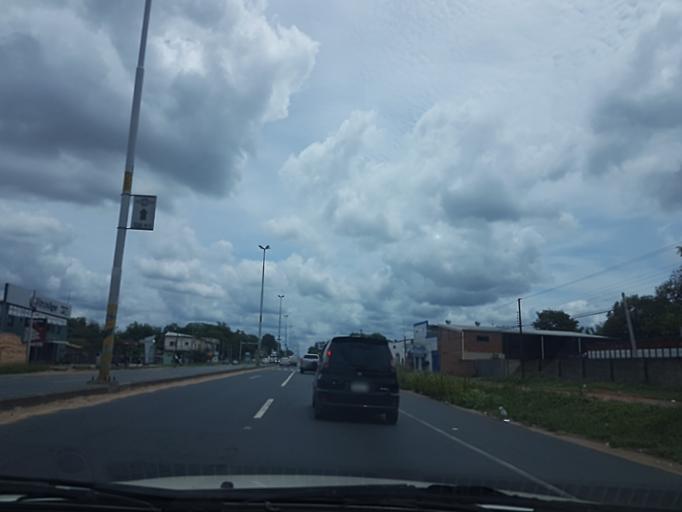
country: PY
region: Central
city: Colonia Mariano Roque Alonso
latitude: -25.1954
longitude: -57.5335
